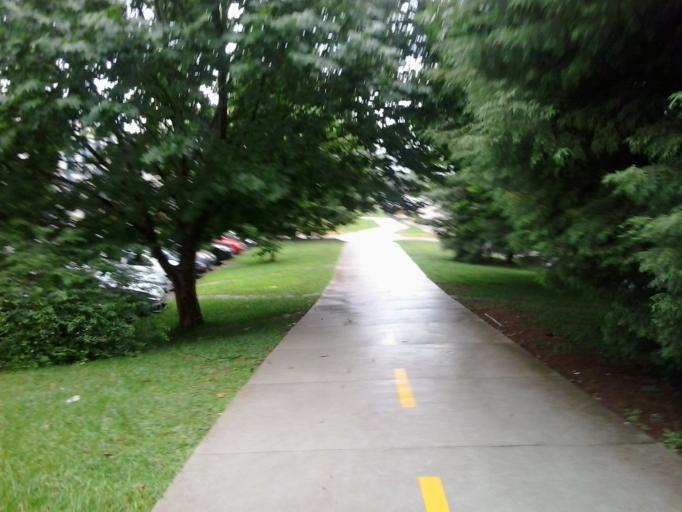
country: BR
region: Rio Grande do Sul
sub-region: Santa Maria
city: Santa Maria
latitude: -29.7190
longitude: -53.7153
